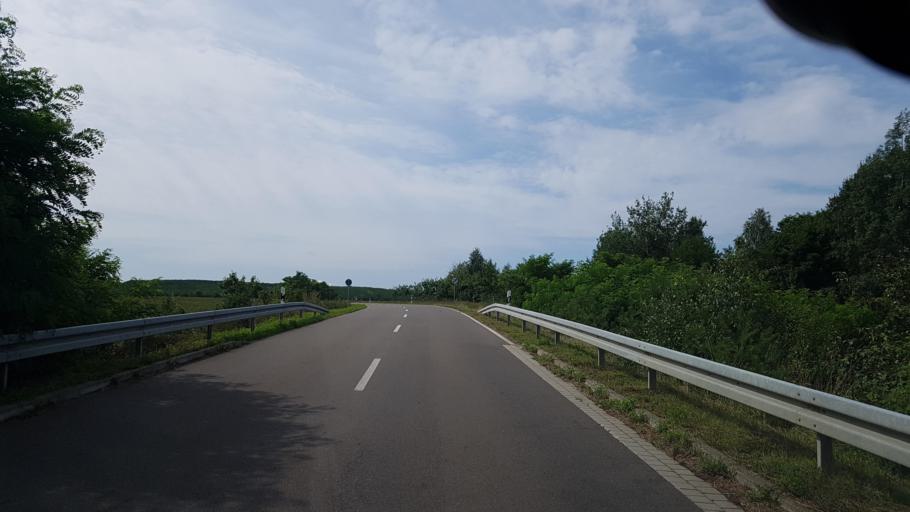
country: DE
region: Brandenburg
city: Drebkau
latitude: 51.6192
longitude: 14.2584
